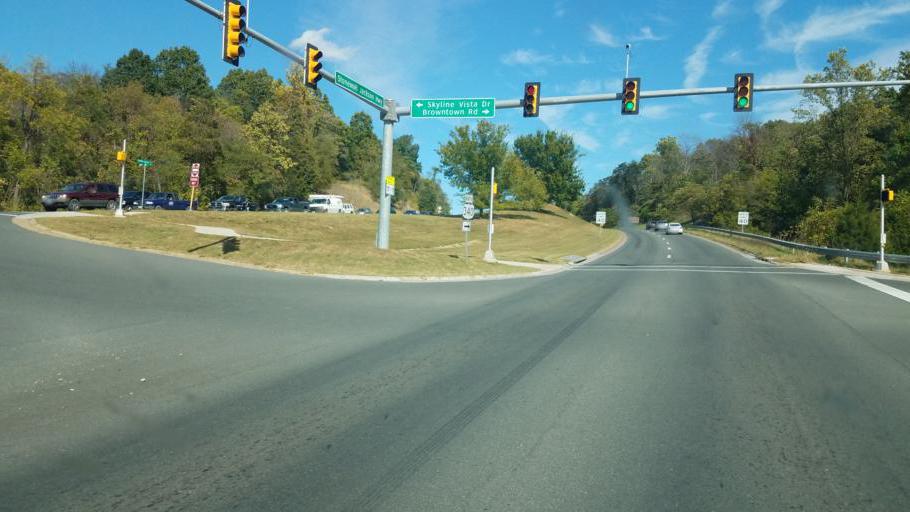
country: US
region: Virginia
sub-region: Warren County
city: Front Royal
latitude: 38.9047
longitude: -78.2052
